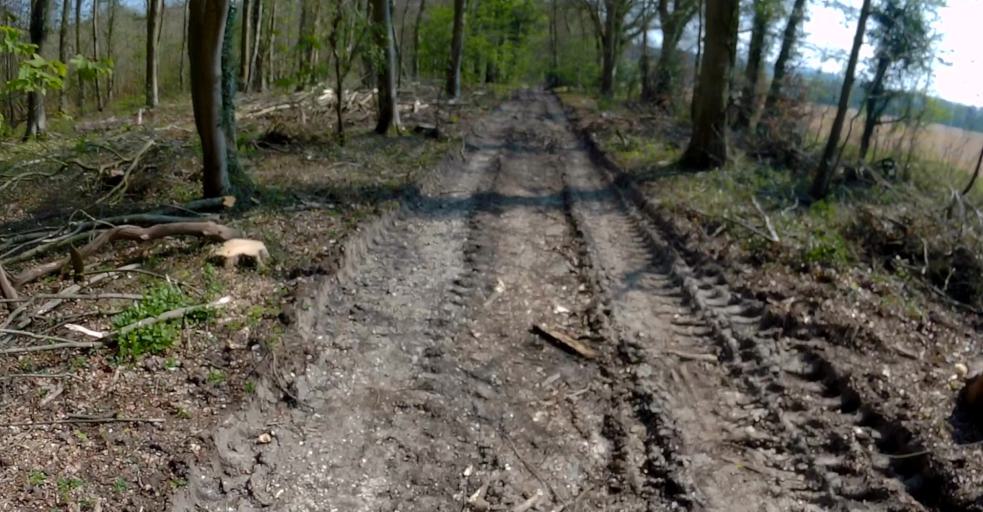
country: GB
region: England
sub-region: Hampshire
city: Overton
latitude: 51.1819
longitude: -1.2418
